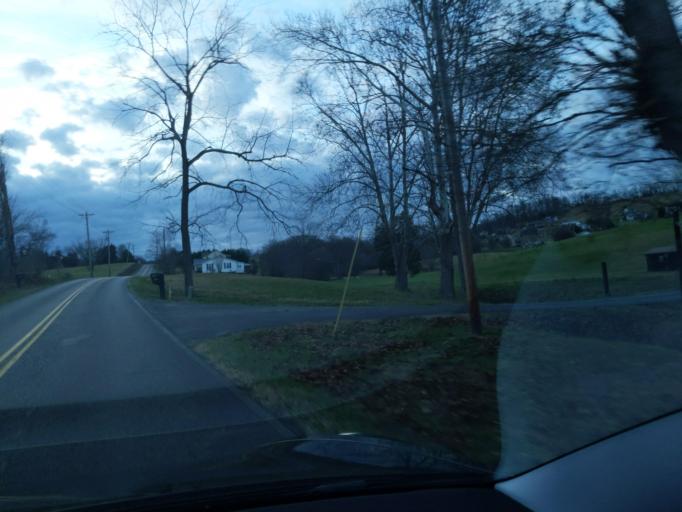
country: US
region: Tennessee
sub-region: Jefferson County
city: White Pine
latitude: 36.1074
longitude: -83.3530
